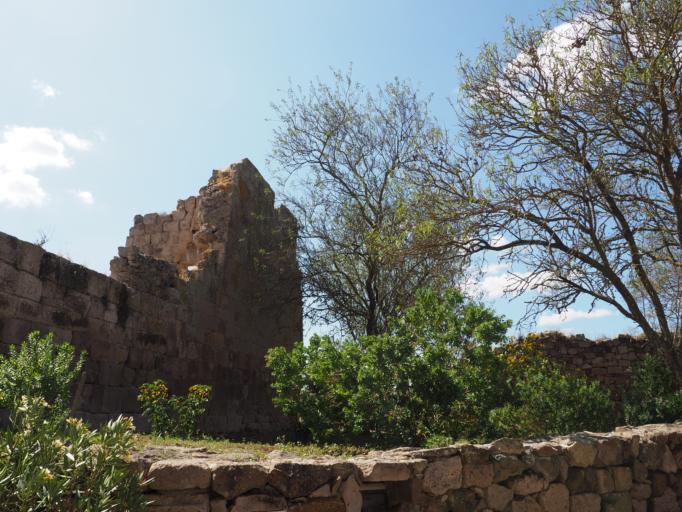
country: IT
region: Sardinia
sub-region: Provincia di Sassari
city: Ardara
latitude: 40.6447
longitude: 8.8925
